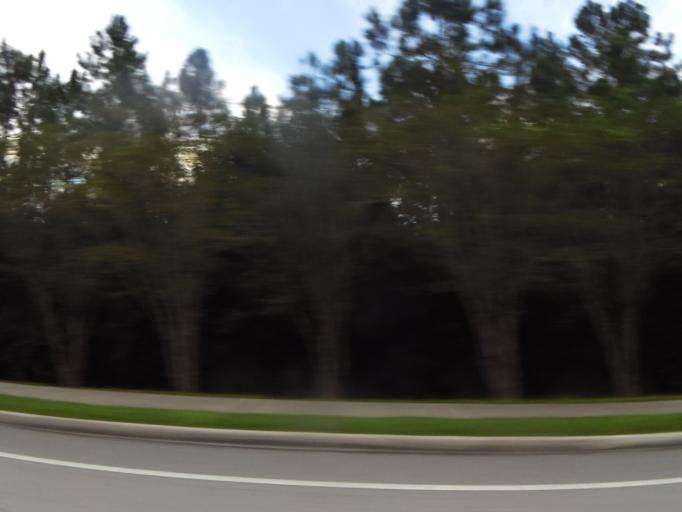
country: US
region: Florida
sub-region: Saint Johns County
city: Fruit Cove
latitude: 30.0862
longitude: -81.5761
